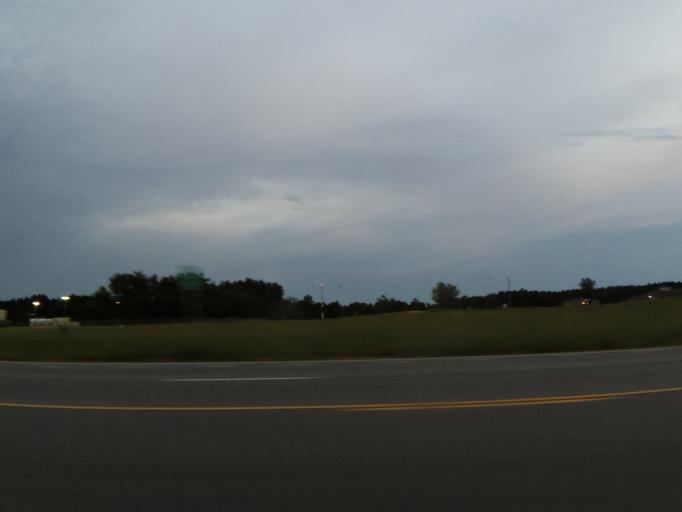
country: US
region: Georgia
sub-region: McDuffie County
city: Thomson
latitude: 33.5259
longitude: -82.5051
